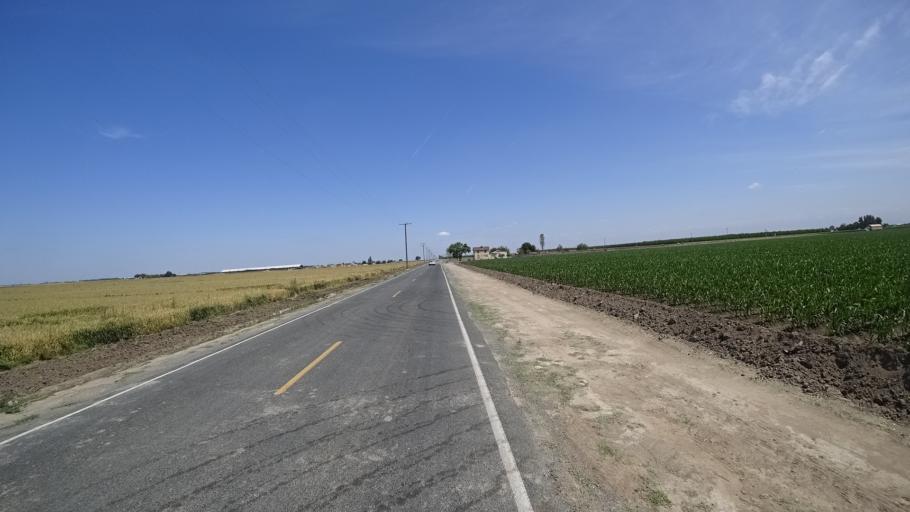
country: US
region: California
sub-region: Tulare County
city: Goshen
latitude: 36.3194
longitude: -119.4932
